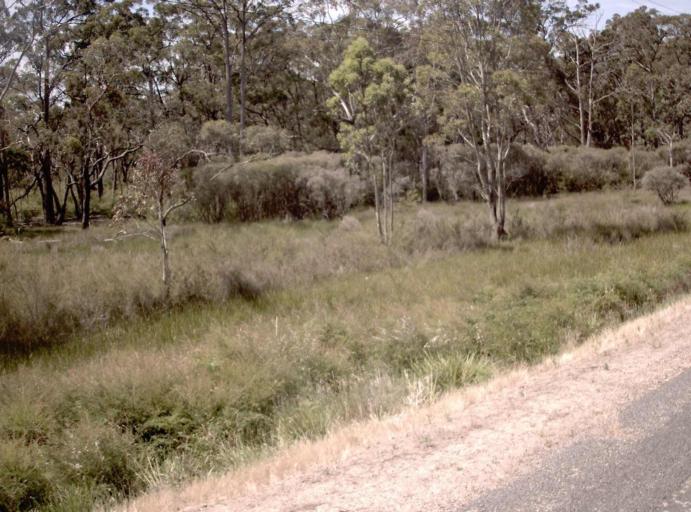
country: AU
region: Victoria
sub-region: Wellington
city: Sale
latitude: -37.9146
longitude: 147.3001
